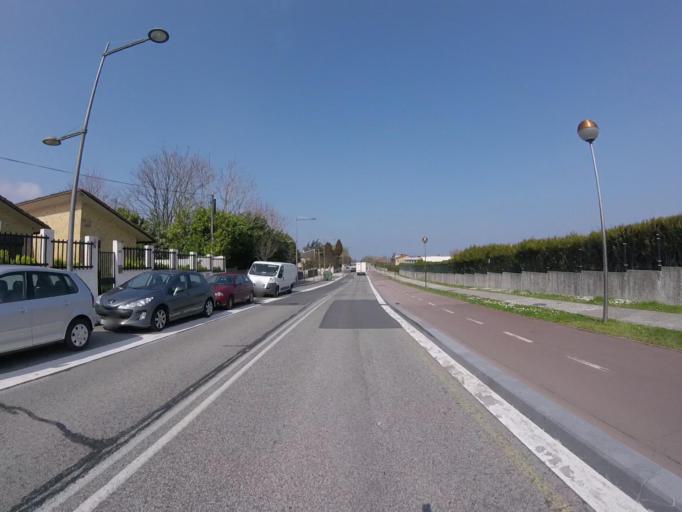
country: ES
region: Basque Country
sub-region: Provincia de Guipuzcoa
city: San Sebastian
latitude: 43.2902
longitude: -1.9903
